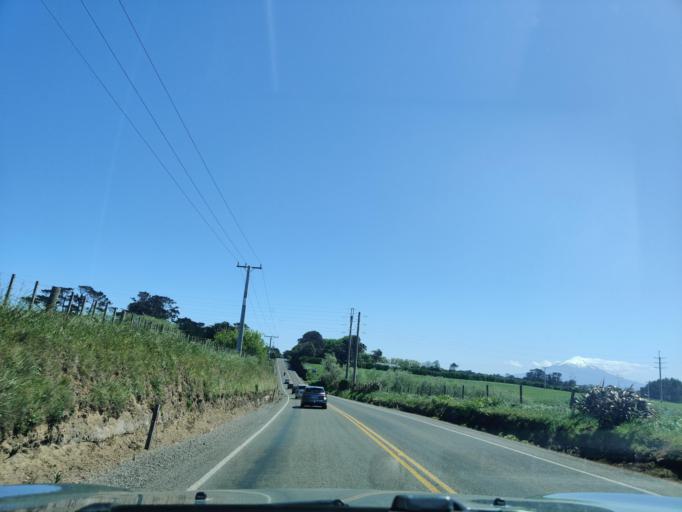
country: NZ
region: Taranaki
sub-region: South Taranaki District
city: Hawera
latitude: -39.6013
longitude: 174.3062
